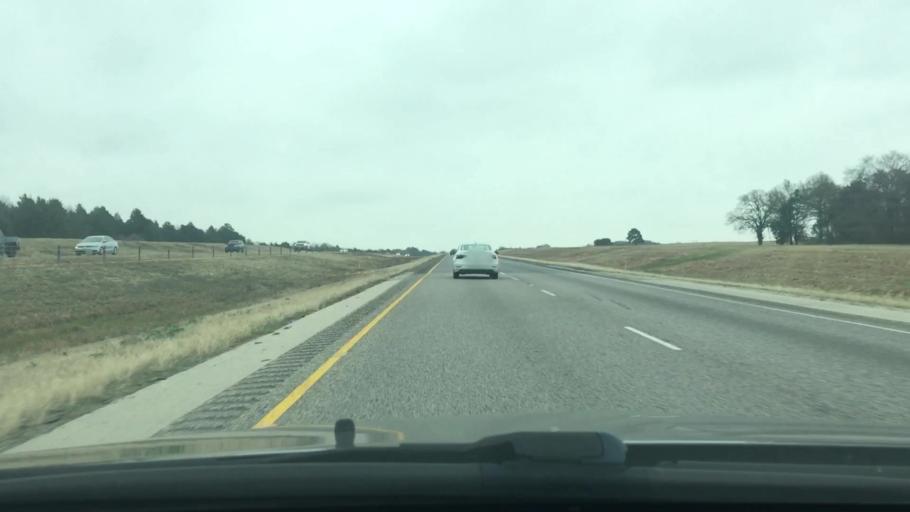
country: US
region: Texas
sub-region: Freestone County
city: Fairfield
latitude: 31.7859
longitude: -96.2408
